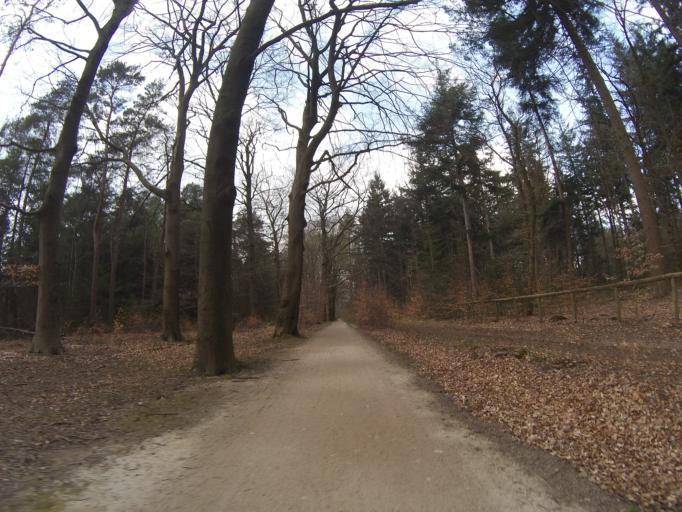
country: NL
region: Utrecht
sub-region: Gemeente Baarn
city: Baarn
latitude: 52.1895
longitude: 5.2316
